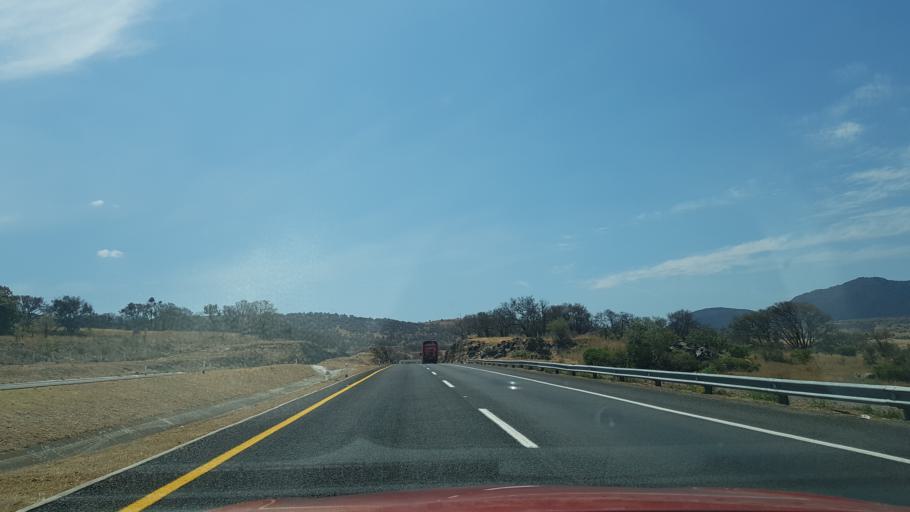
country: MX
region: Michoacan
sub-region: Maravatio
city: Santiago Puriatzicuaro
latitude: 19.9083
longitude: -100.5431
